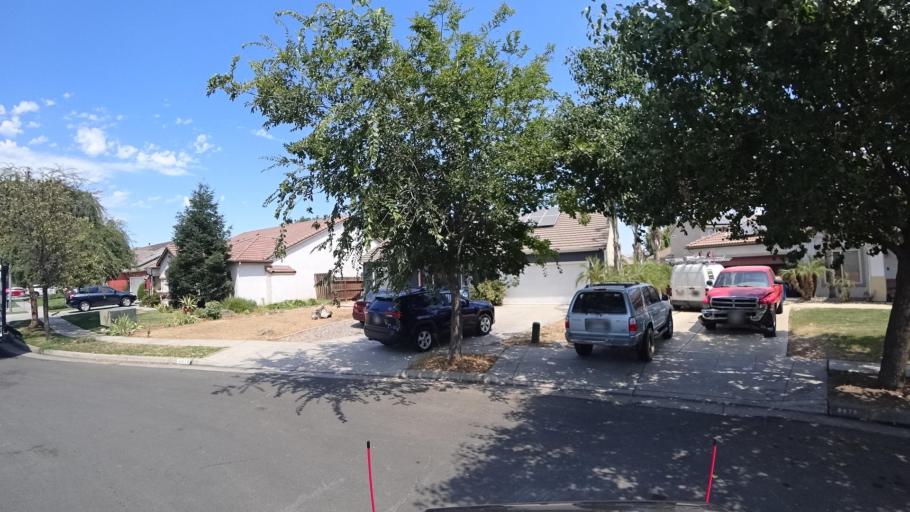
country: US
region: California
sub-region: Fresno County
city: Tarpey Village
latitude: 36.7812
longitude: -119.6798
